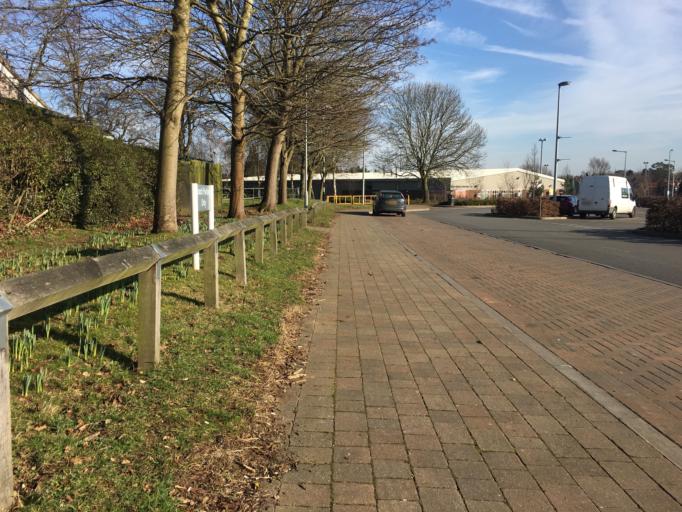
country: GB
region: England
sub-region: Warwickshire
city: Rugby
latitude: 52.3667
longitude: -1.2548
